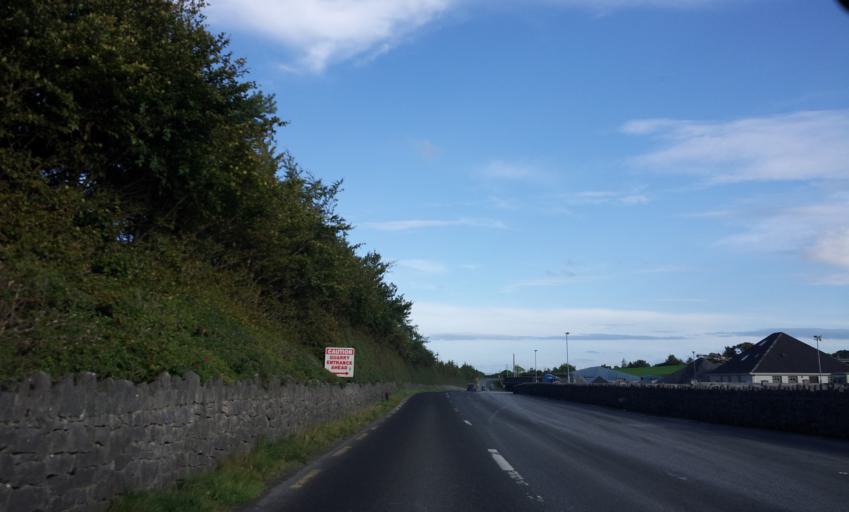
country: IE
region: Munster
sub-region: An Clar
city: Ennis
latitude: 52.9018
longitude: -9.0375
